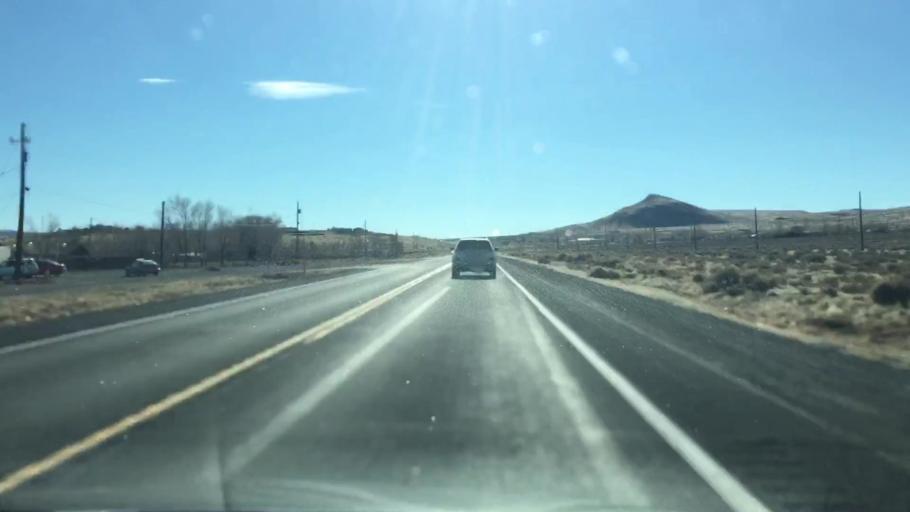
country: US
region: Nevada
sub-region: Lyon County
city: Silver Springs
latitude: 39.3506
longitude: -119.2389
